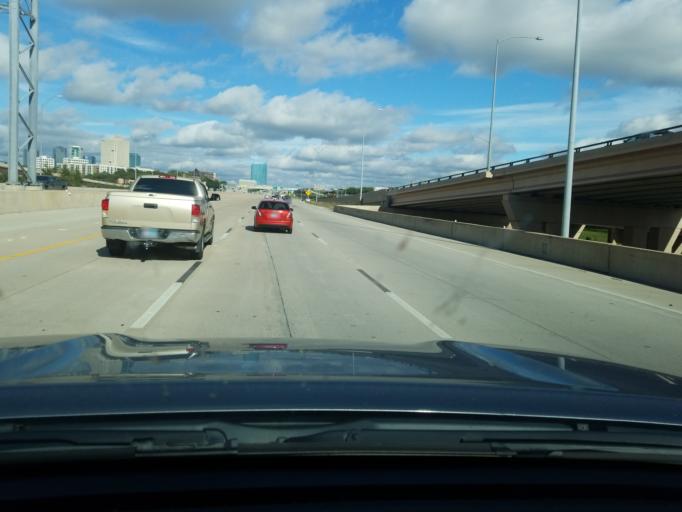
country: US
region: Texas
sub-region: Tarrant County
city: Fort Worth
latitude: 32.7387
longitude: -97.3506
